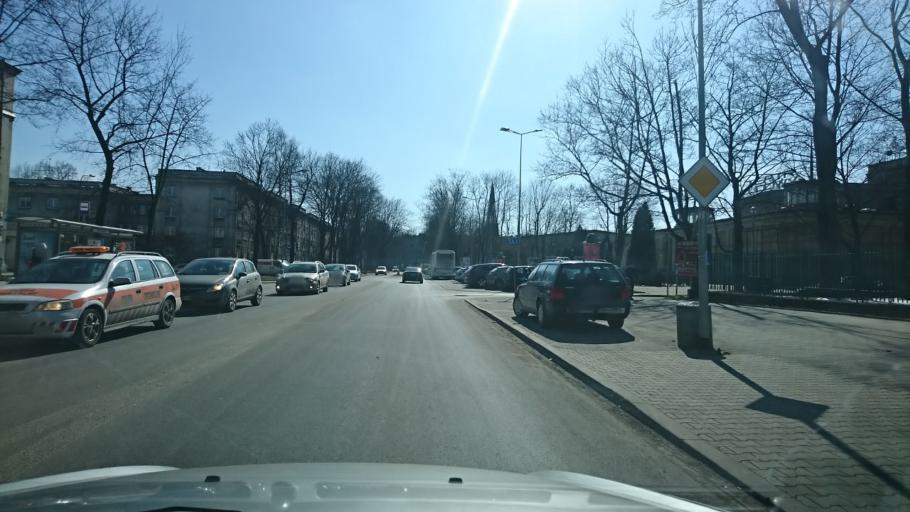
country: PL
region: Lesser Poland Voivodeship
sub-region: Powiat wielicki
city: Kokotow
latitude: 50.0814
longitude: 20.0335
